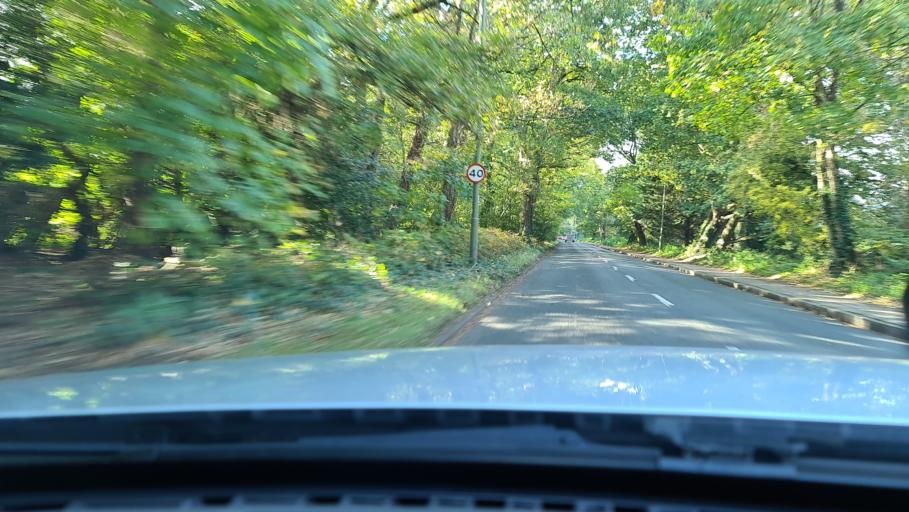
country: GB
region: England
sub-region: Surrey
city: Walton-on-Thames
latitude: 51.3697
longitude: -0.4150
